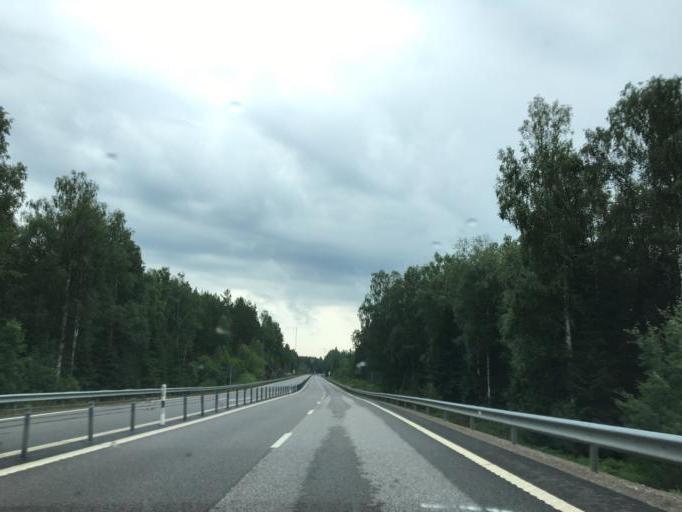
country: SE
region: OEstergoetland
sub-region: Norrkopings Kommun
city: Jursla
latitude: 58.8052
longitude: 16.1518
